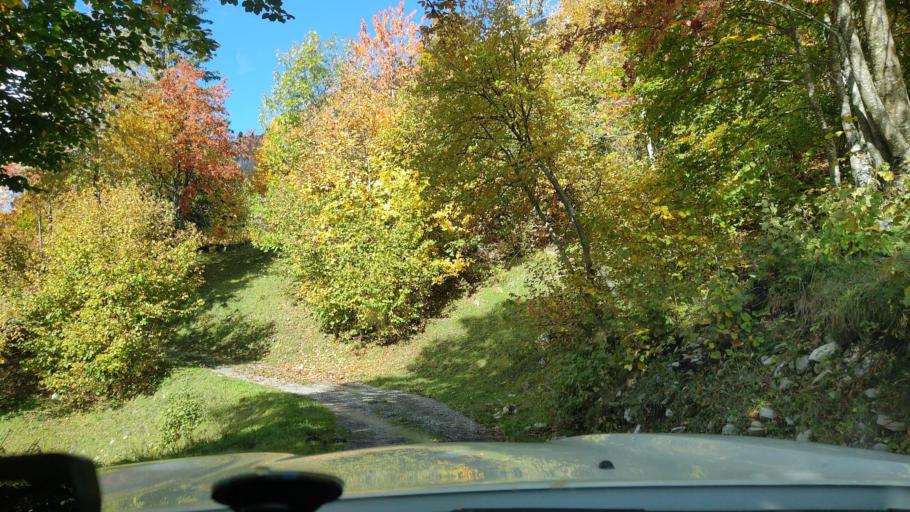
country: FR
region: Rhone-Alpes
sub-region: Departement de la Haute-Savoie
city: La Clusaz
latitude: 45.8722
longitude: 6.4851
